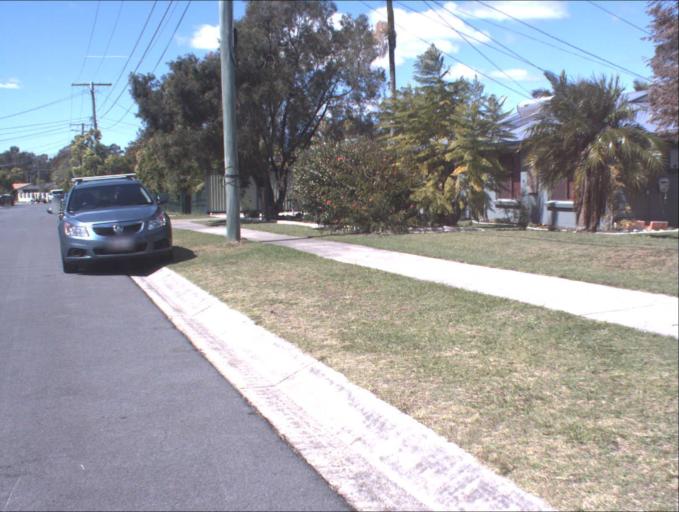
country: AU
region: Queensland
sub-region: Logan
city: Logan Reserve
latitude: -27.6896
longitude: 153.0899
